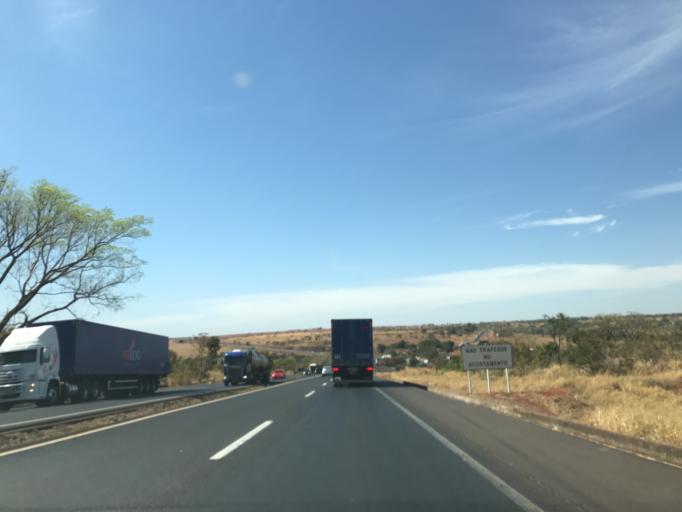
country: BR
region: Minas Gerais
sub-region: Monte Alegre De Minas
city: Monte Alegre de Minas
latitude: -18.8723
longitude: -49.0615
